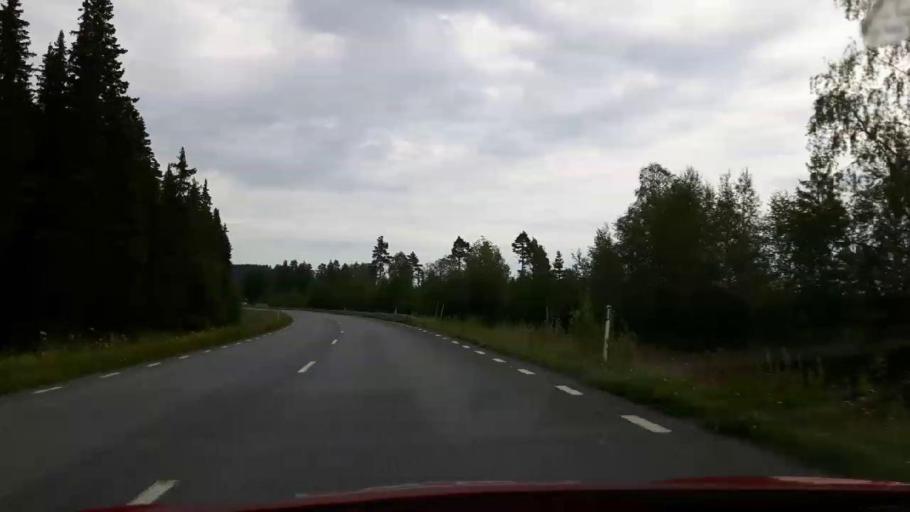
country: SE
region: Jaemtland
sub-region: Stroemsunds Kommun
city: Stroemsund
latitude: 63.5411
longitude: 15.3656
